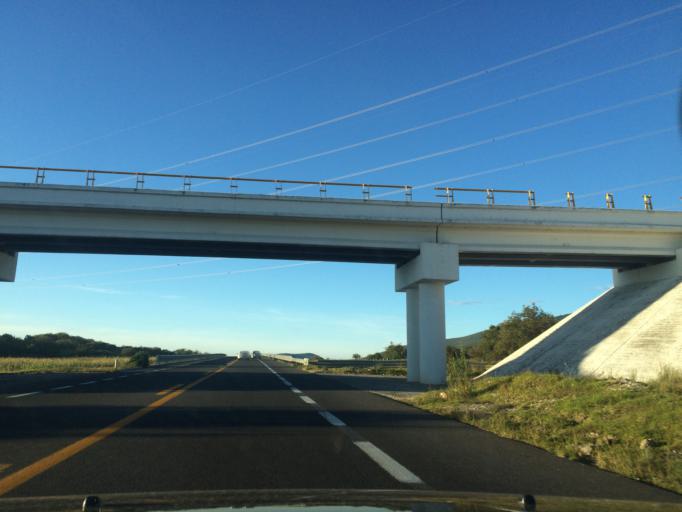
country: MX
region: Puebla
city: Morelos Canada
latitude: 18.7032
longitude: -97.4666
